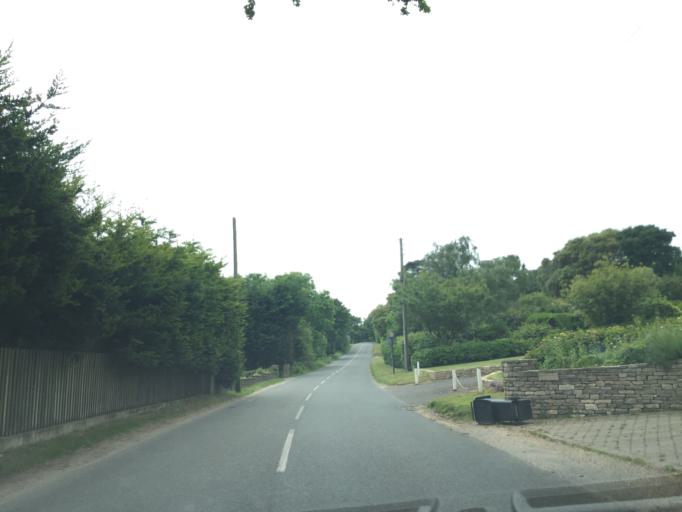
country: GB
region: England
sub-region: Dorset
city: Swanage
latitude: 50.6403
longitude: -1.9536
